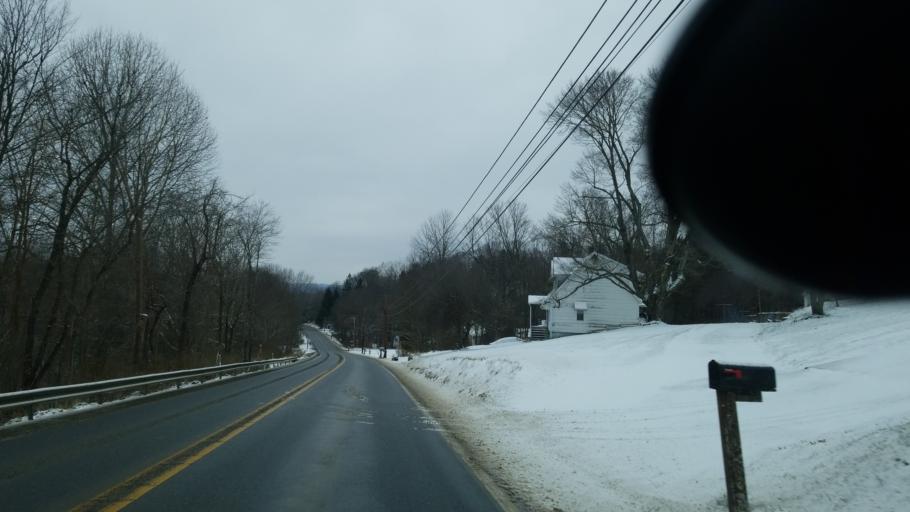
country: US
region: Pennsylvania
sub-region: Jefferson County
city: Albion
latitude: 40.9369
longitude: -78.9209
